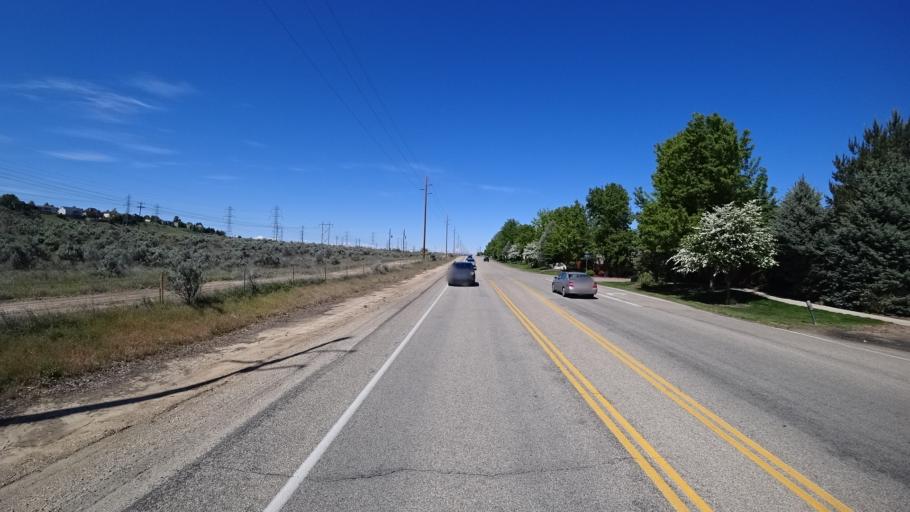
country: US
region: Idaho
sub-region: Ada County
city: Boise
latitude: 43.5600
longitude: -116.1381
